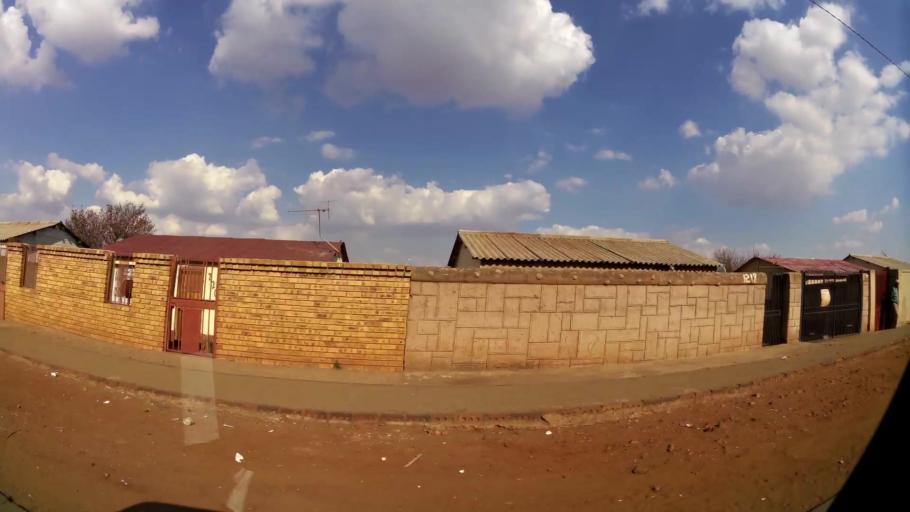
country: ZA
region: Gauteng
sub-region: City of Johannesburg Metropolitan Municipality
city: Soweto
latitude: -26.2180
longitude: 27.8661
